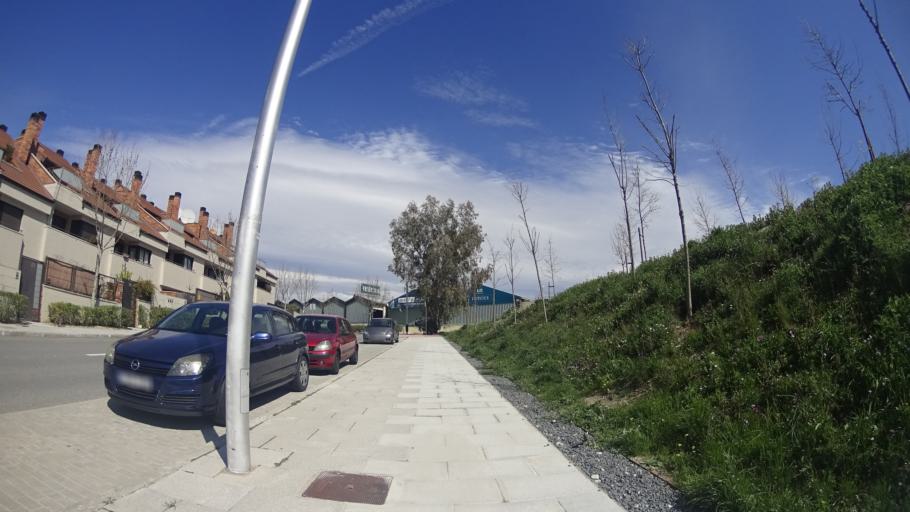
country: ES
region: Madrid
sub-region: Provincia de Madrid
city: Torrelodones
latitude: 40.5665
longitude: -3.9162
